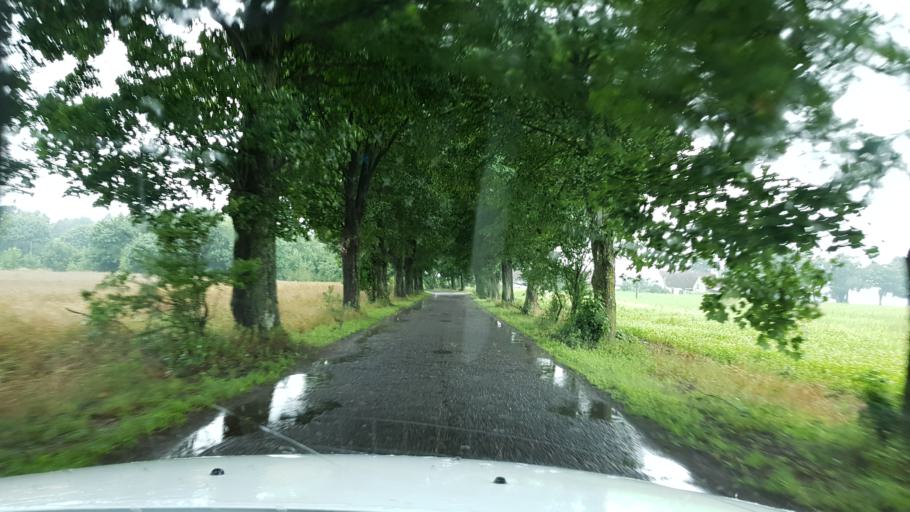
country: PL
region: West Pomeranian Voivodeship
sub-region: Powiat gryficki
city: Brojce
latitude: 53.9516
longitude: 15.4334
